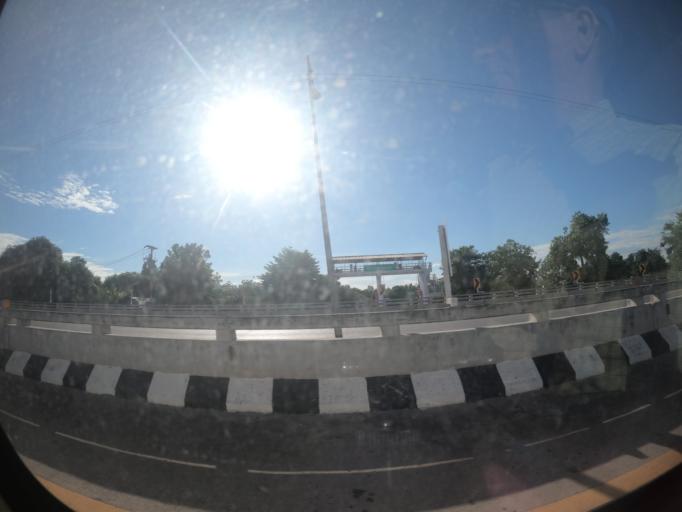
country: TH
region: Nakhon Nayok
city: Ongkharak
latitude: 14.1463
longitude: 100.9852
